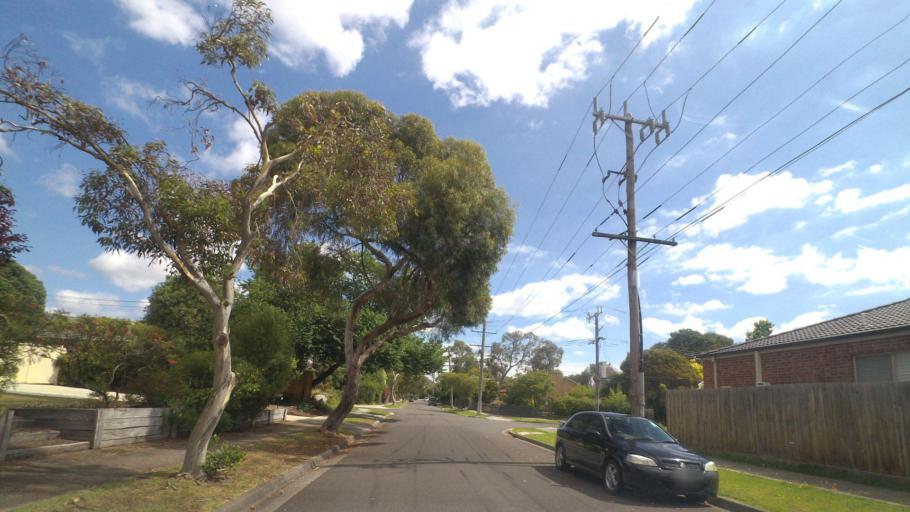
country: AU
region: Victoria
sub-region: Knox
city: Bayswater
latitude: -37.8641
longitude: 145.2583
